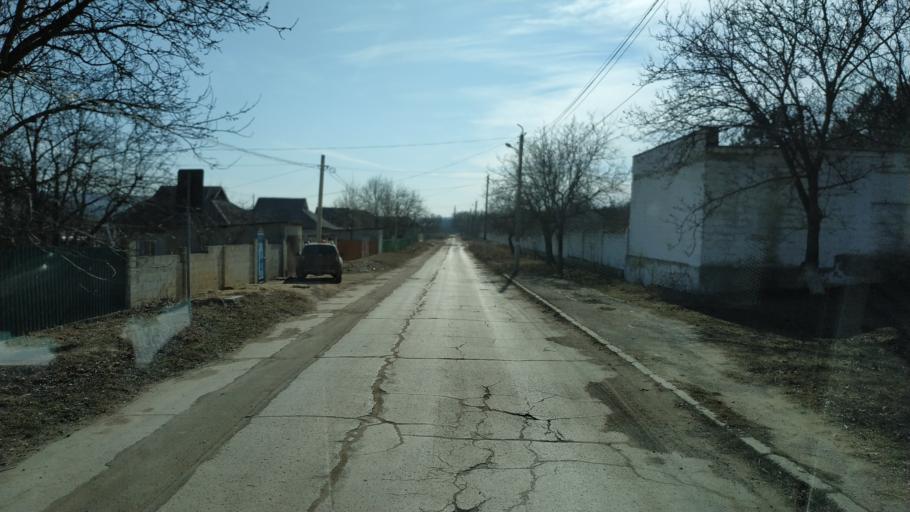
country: MD
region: Nisporeni
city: Nisporeni
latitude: 47.0663
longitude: 28.1732
